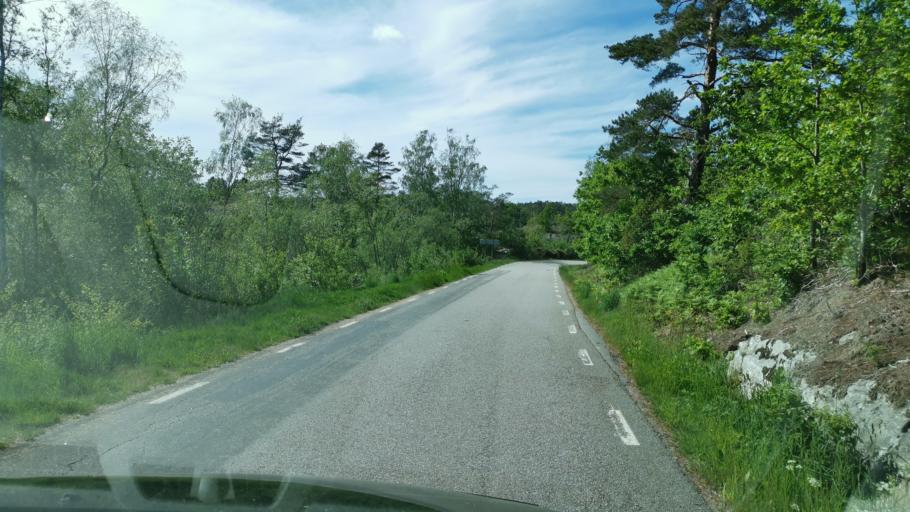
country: SE
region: Vaestra Goetaland
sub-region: Orust
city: Henan
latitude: 58.2649
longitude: 11.6090
